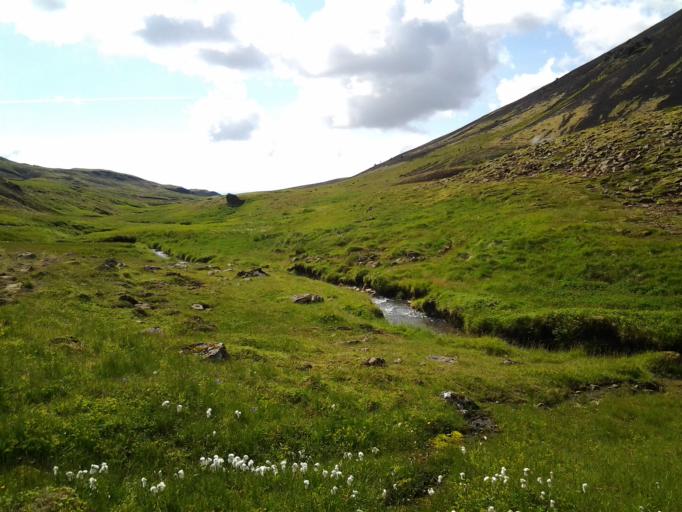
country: IS
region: South
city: Hveragerdi
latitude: 64.0456
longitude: -21.2190
